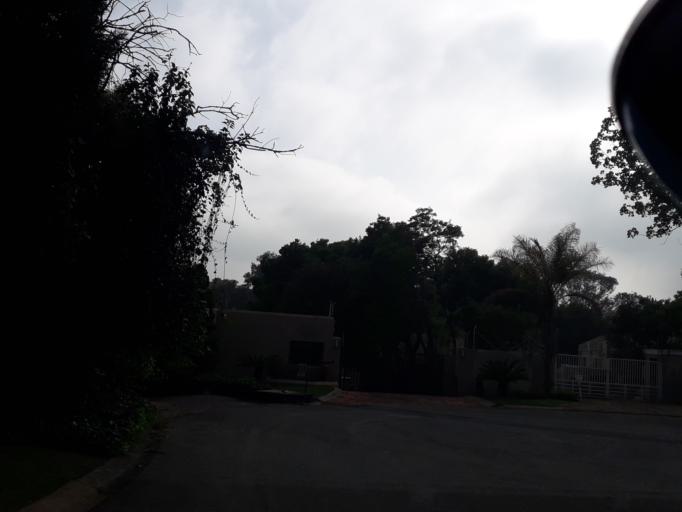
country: ZA
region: Gauteng
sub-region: City of Johannesburg Metropolitan Municipality
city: Midrand
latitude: -26.0686
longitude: 28.0656
